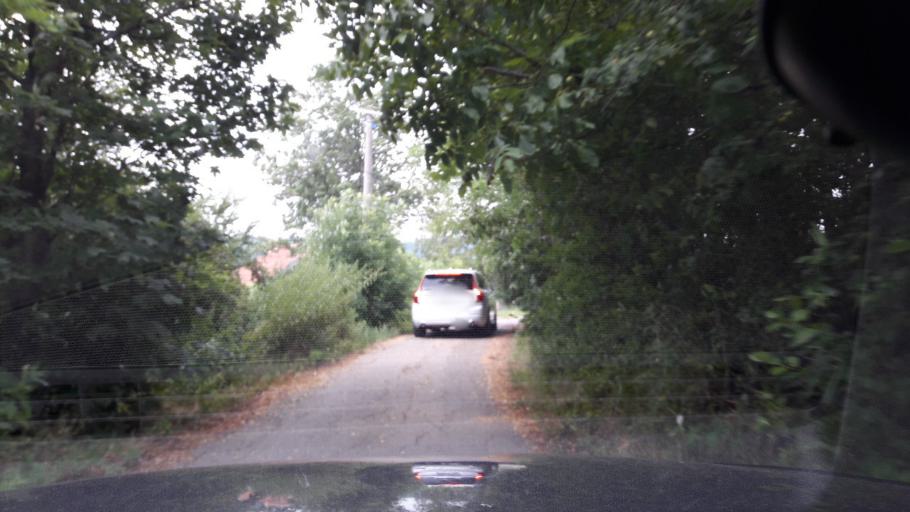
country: RS
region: Central Serbia
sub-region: Belgrade
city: Sopot
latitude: 44.6003
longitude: 20.6008
